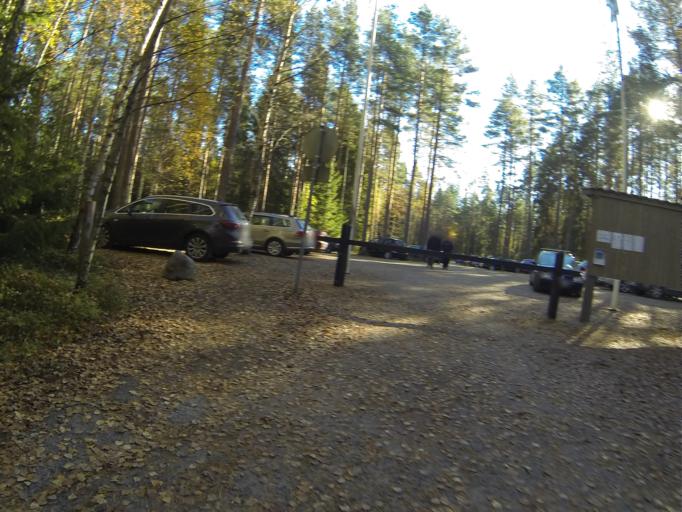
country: FI
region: Varsinais-Suomi
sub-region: Salo
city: Saerkisalo
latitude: 60.2099
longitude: 22.9379
